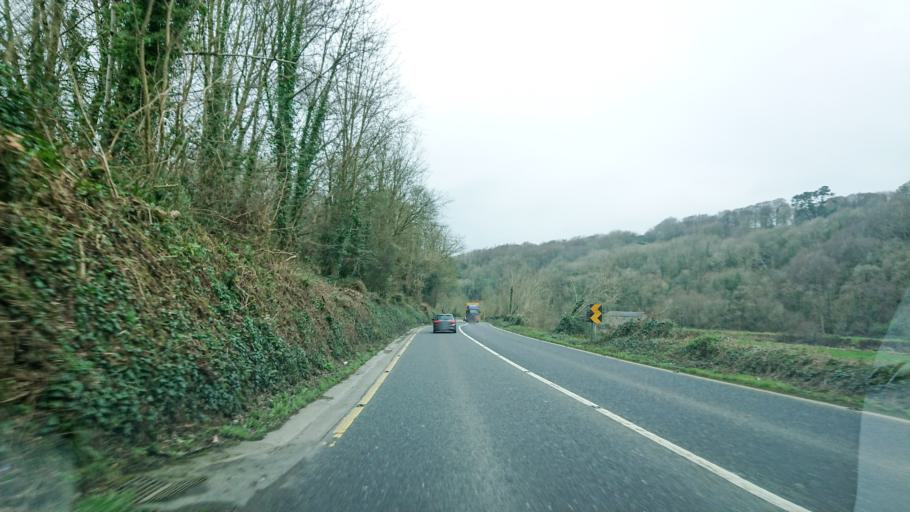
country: IE
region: Munster
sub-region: County Cork
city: Bandon
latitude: 51.7671
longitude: -8.6718
